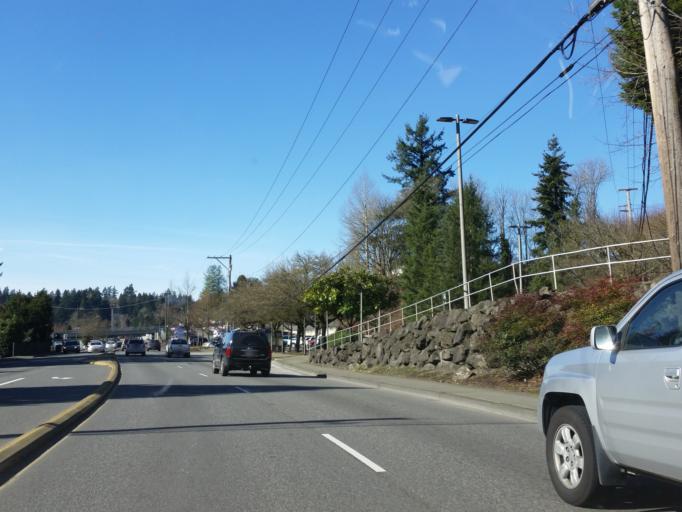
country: US
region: Washington
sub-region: King County
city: Bothell
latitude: 47.7593
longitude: -122.1999
